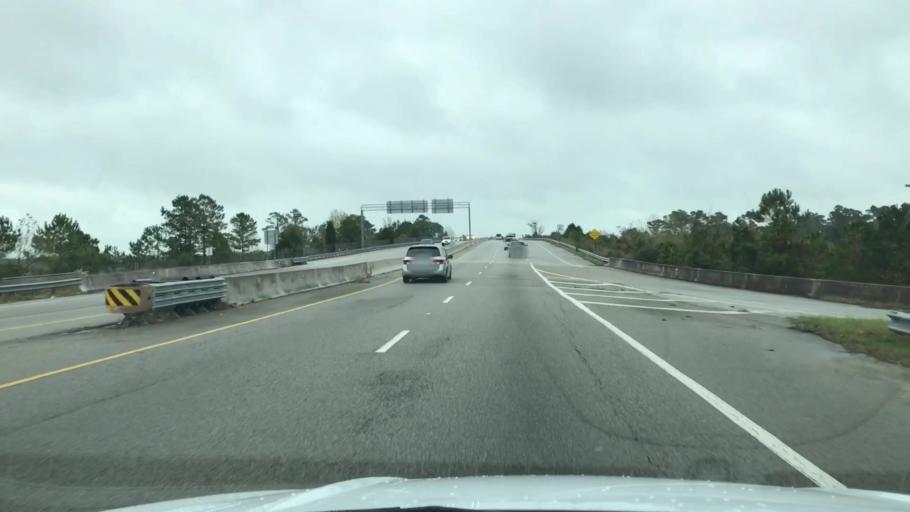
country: US
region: South Carolina
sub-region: Horry County
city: Myrtle Beach
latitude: 33.7527
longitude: -78.8516
